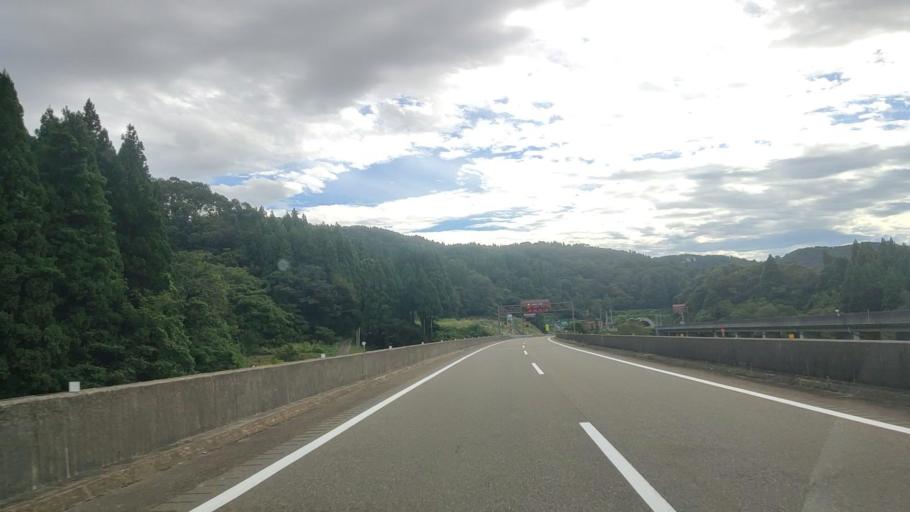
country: JP
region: Niigata
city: Joetsu
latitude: 37.1466
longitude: 138.1940
